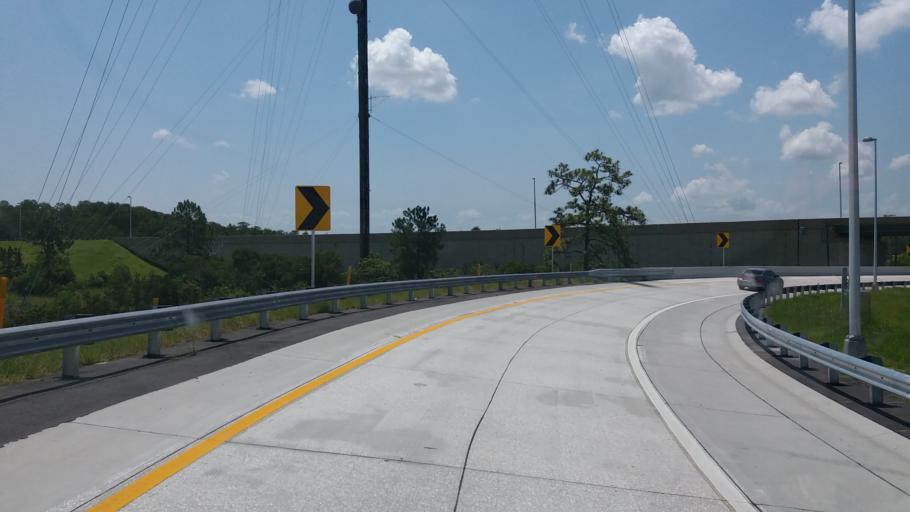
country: US
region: Florida
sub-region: Orange County
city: Southchase
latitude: 28.3677
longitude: -81.3878
